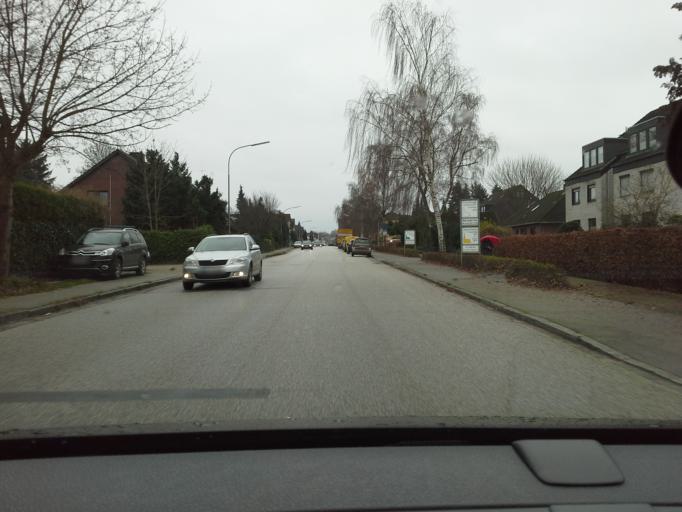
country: DE
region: Schleswig-Holstein
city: Quickborn
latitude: 53.7374
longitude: 9.8917
